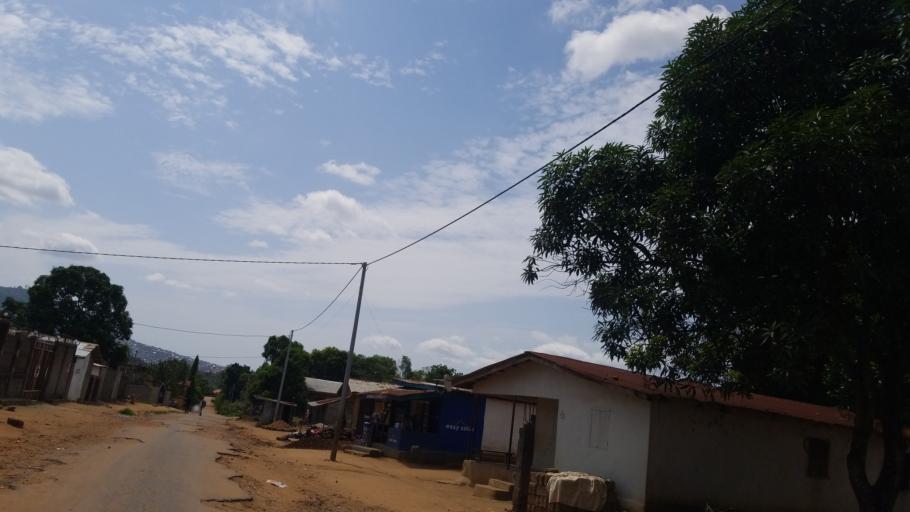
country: SL
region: Western Area
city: Waterloo
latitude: 8.3145
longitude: -13.0563
